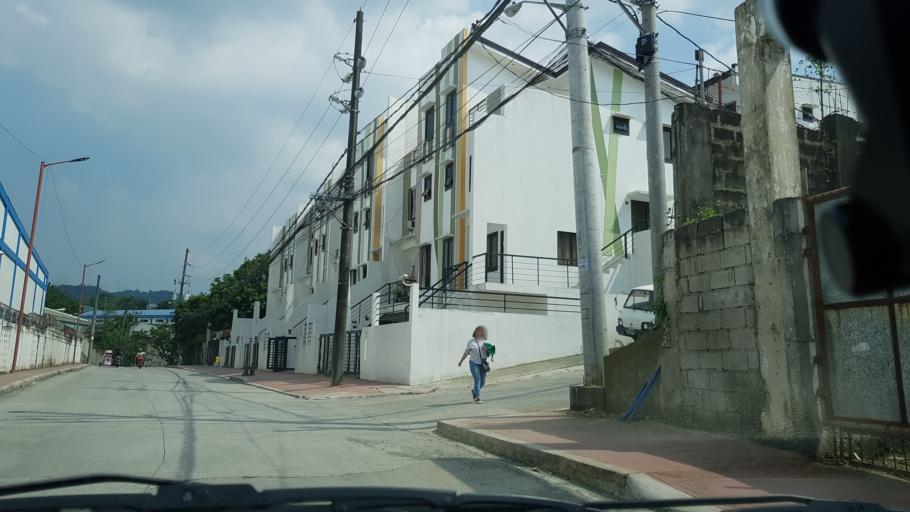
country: PH
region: Calabarzon
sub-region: Province of Rizal
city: Antipolo
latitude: 14.6619
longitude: 121.1268
